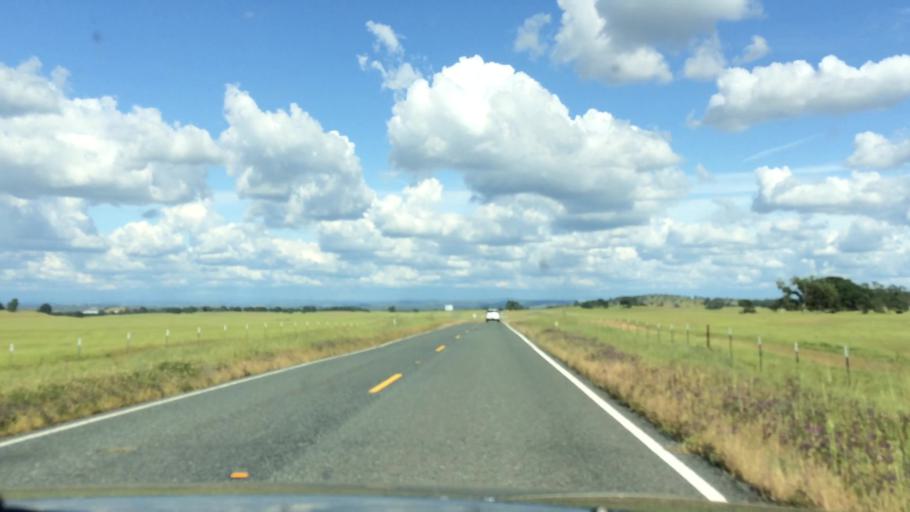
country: US
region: California
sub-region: Amador County
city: Ione
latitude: 38.3863
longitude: -121.0355
